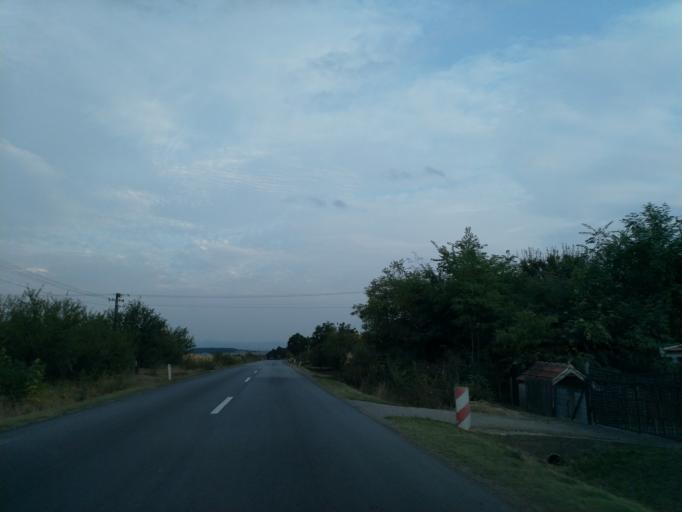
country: RS
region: Central Serbia
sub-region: Sumadijski Okrug
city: Kragujevac
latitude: 44.1225
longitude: 20.8268
